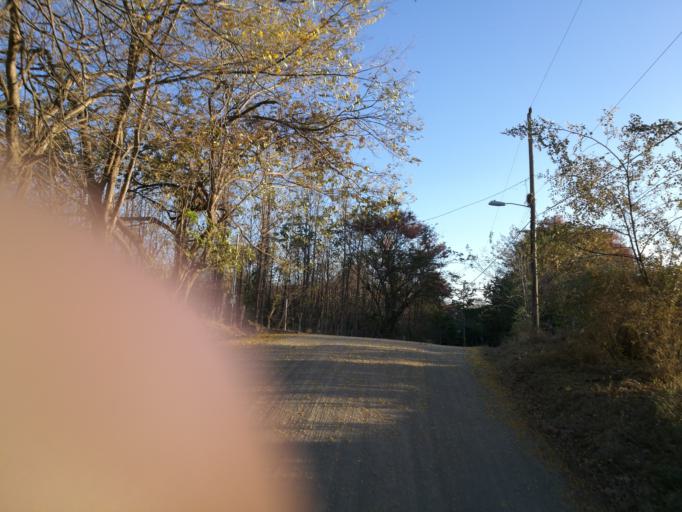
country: CR
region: Guanacaste
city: Nandayure
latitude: 10.0980
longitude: -85.1851
